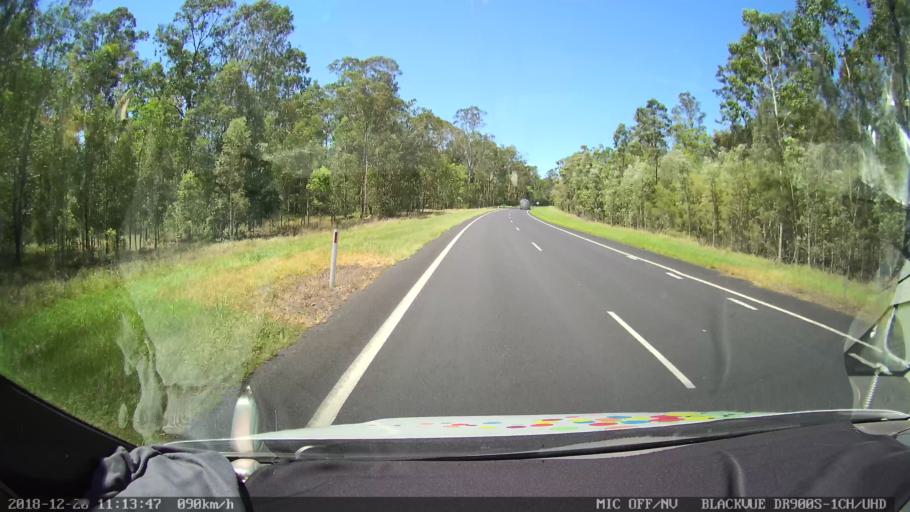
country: AU
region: New South Wales
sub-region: Richmond Valley
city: Casino
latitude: -28.9921
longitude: 153.0117
